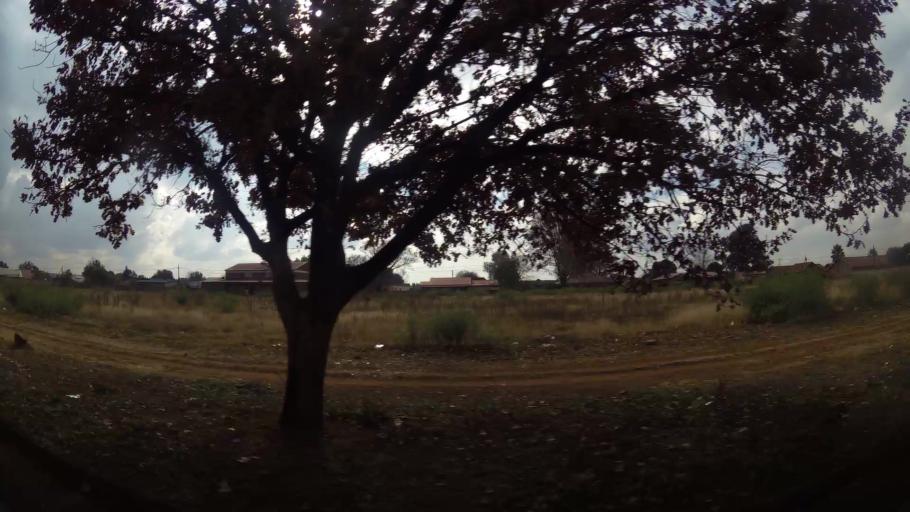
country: ZA
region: Gauteng
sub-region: Sedibeng District Municipality
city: Meyerton
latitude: -26.5975
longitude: 27.9925
